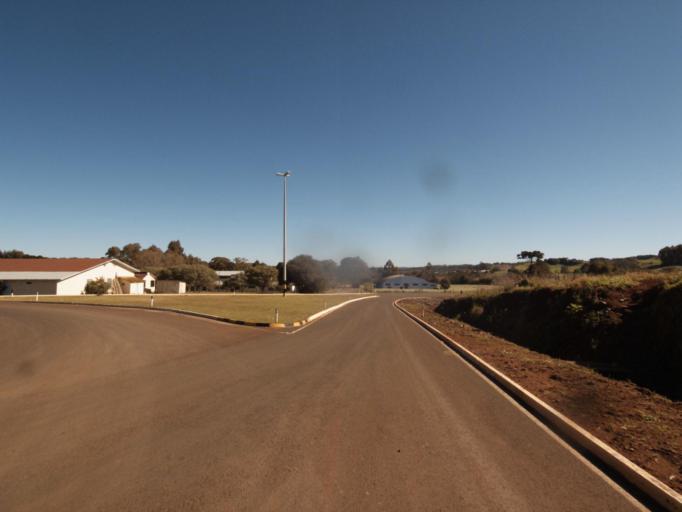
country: AR
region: Misiones
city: Bernardo de Irigoyen
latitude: -26.6139
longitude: -53.6738
